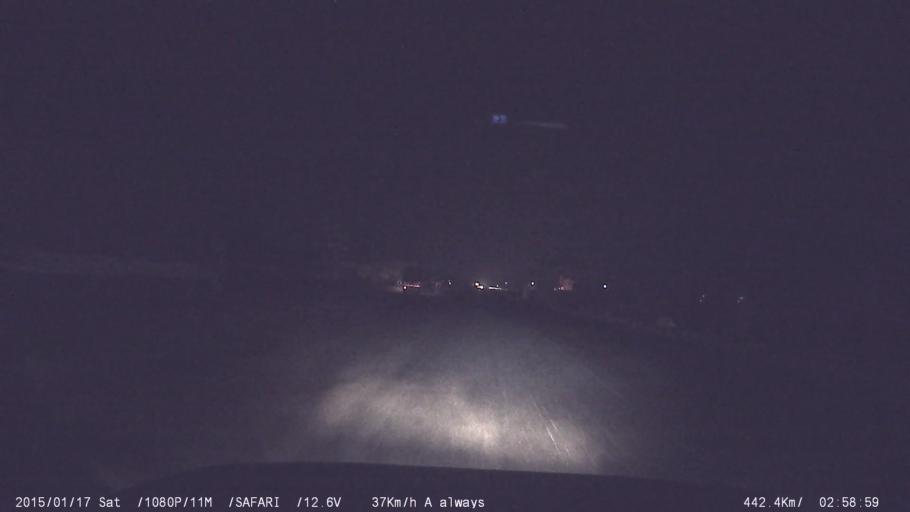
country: IN
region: Tamil Nadu
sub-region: Krishnagiri
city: Hosur
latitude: 12.7755
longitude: 77.7796
